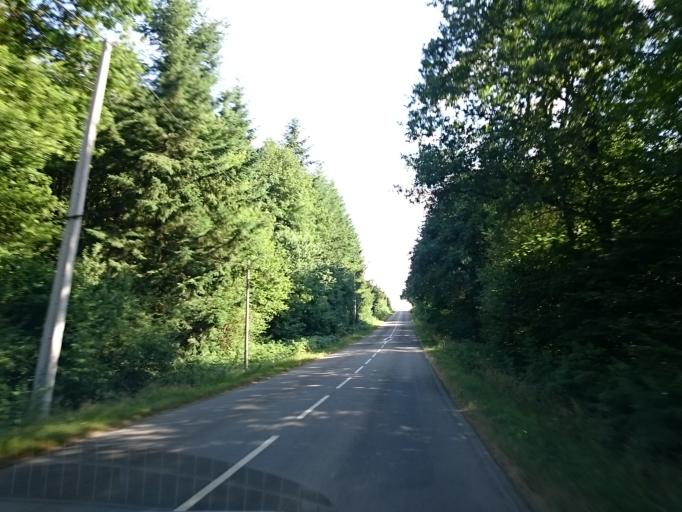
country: FR
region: Brittany
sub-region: Departement d'Ille-et-Vilaine
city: Pance
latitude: 47.9071
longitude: -1.6160
